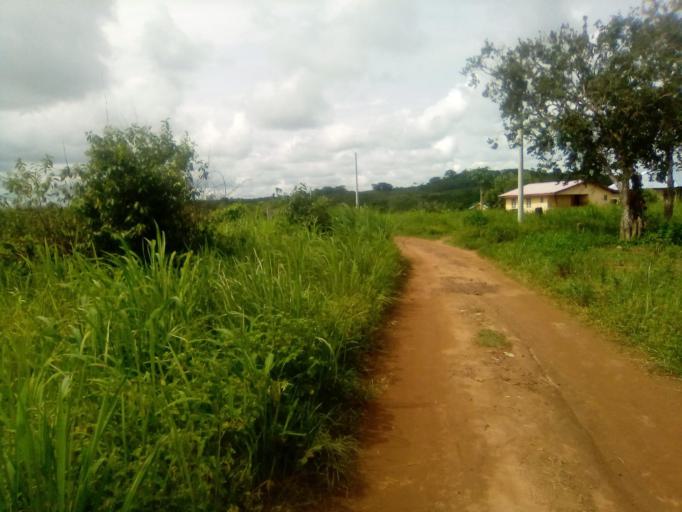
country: SL
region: Southern Province
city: Moyamba
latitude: 8.1462
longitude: -12.4309
